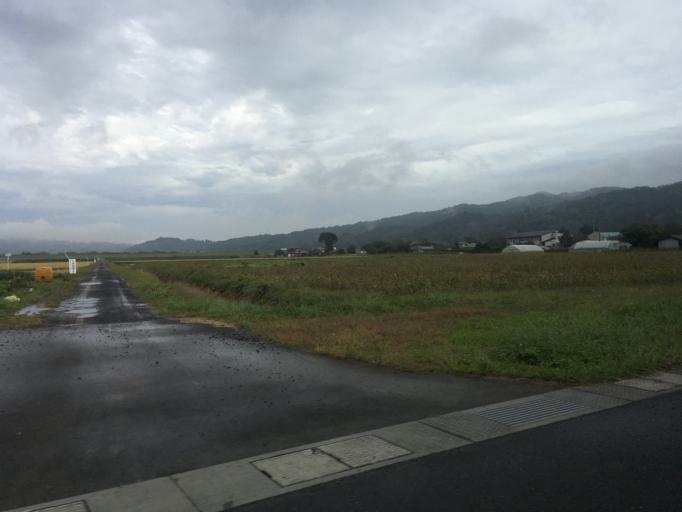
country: JP
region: Iwate
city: Ichinoseki
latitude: 38.8323
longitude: 141.2506
